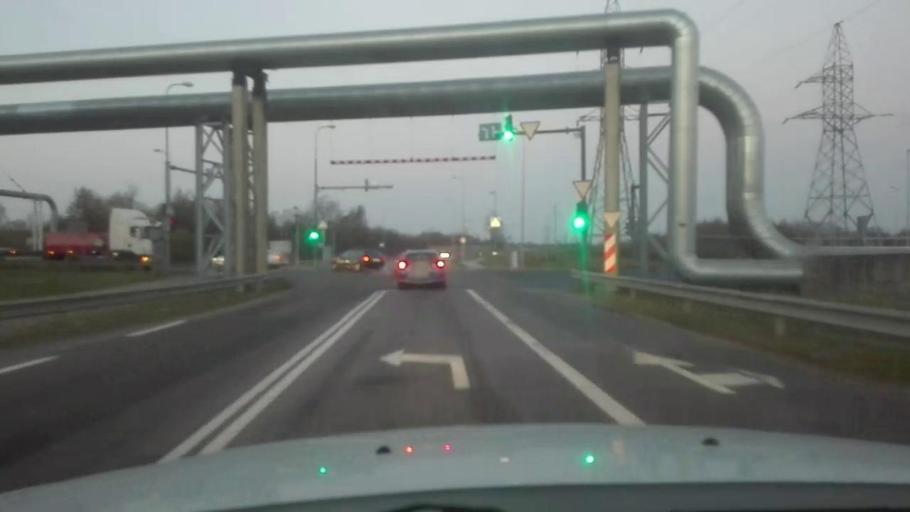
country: EE
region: Harju
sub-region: Maardu linn
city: Maardu
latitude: 59.4793
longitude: 24.9926
